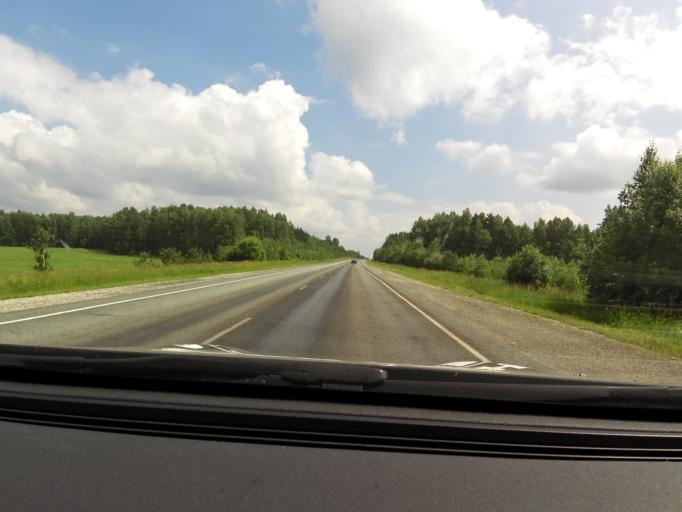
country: RU
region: Sverdlovsk
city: Achit
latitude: 56.8516
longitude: 57.7243
